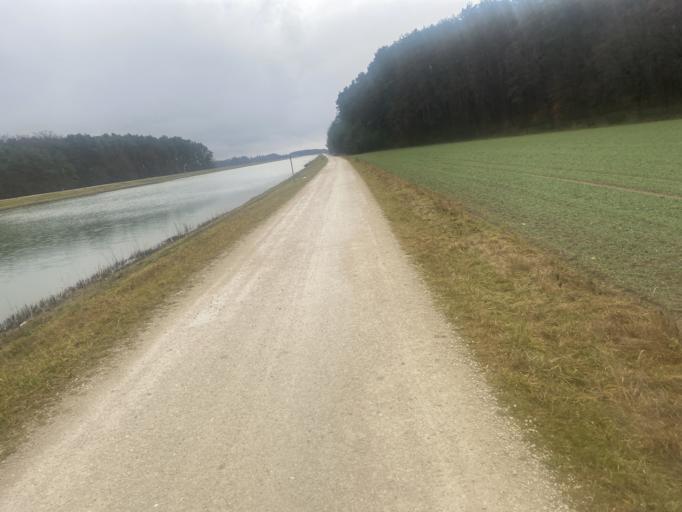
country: DE
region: Bavaria
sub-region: Upper Franconia
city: Hausen
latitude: 49.6791
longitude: 11.0299
